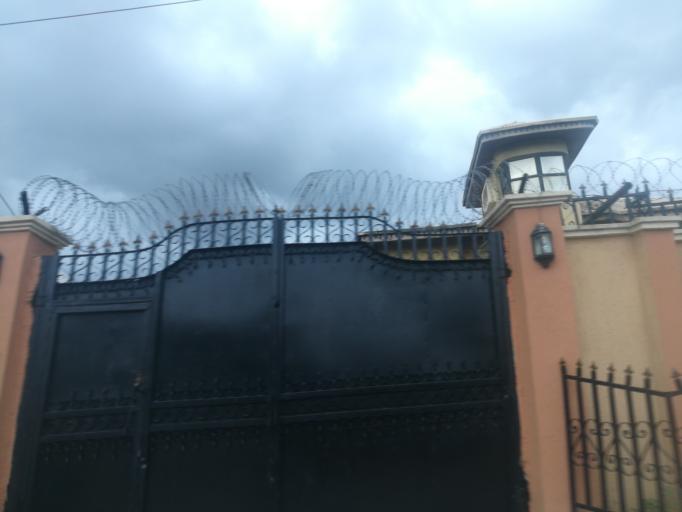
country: NG
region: Lagos
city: Ojota
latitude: 6.5626
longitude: 3.3840
